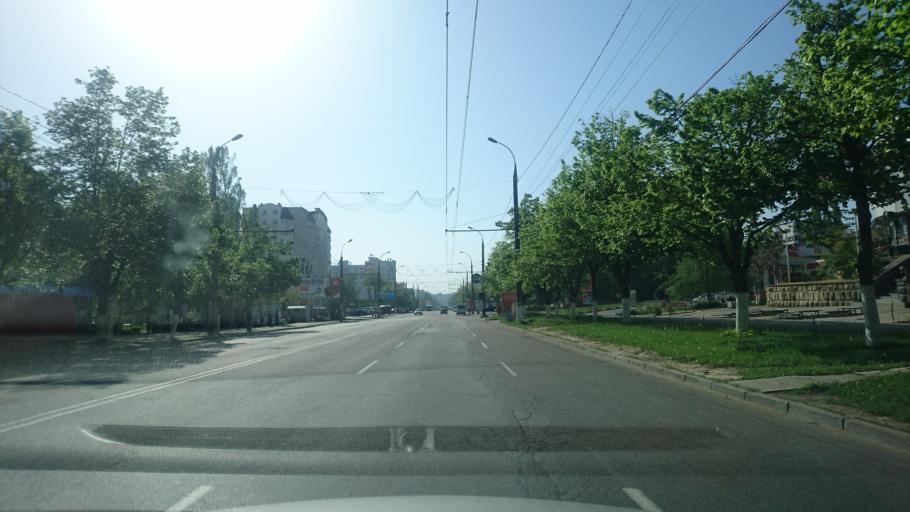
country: MD
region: Chisinau
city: Vatra
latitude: 47.0359
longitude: 28.7747
